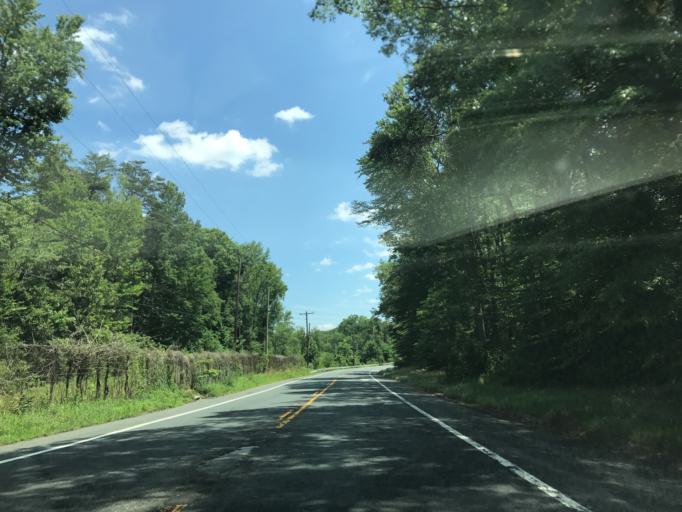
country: US
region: Maryland
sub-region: Anne Arundel County
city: Maryland City
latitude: 39.0439
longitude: -76.8000
